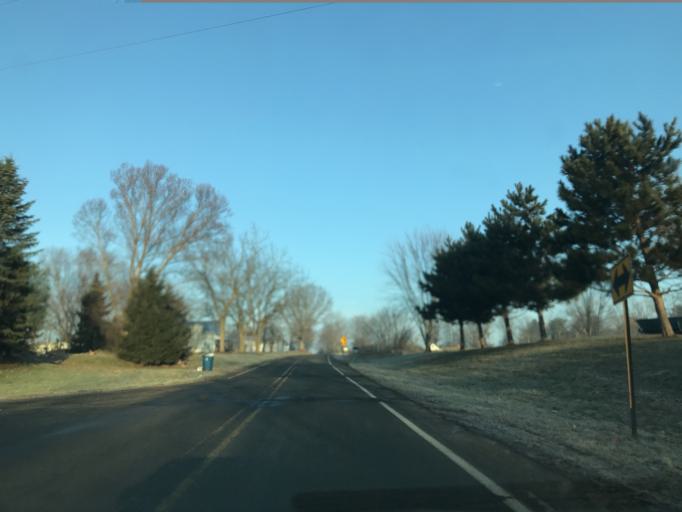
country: US
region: Michigan
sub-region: Ingham County
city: Leslie
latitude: 42.4038
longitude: -84.4859
